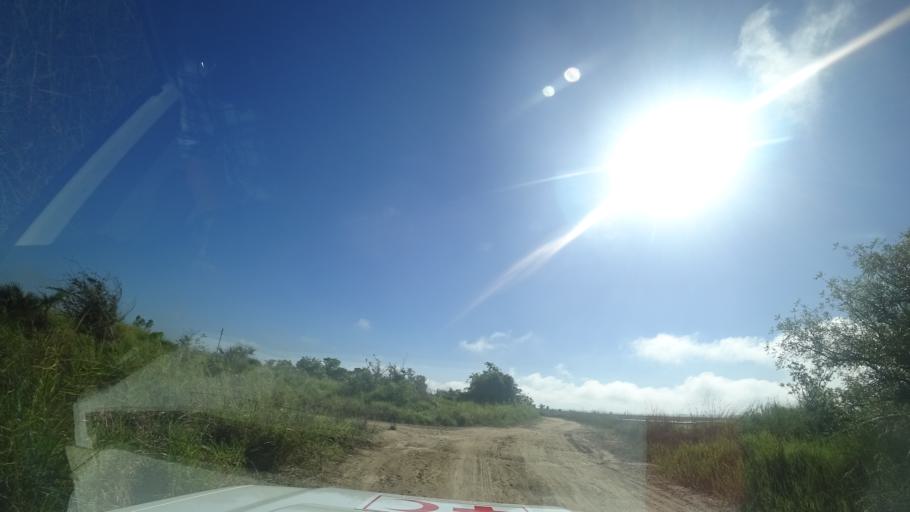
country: MZ
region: Sofala
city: Dondo
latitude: -19.4284
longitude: 34.5608
